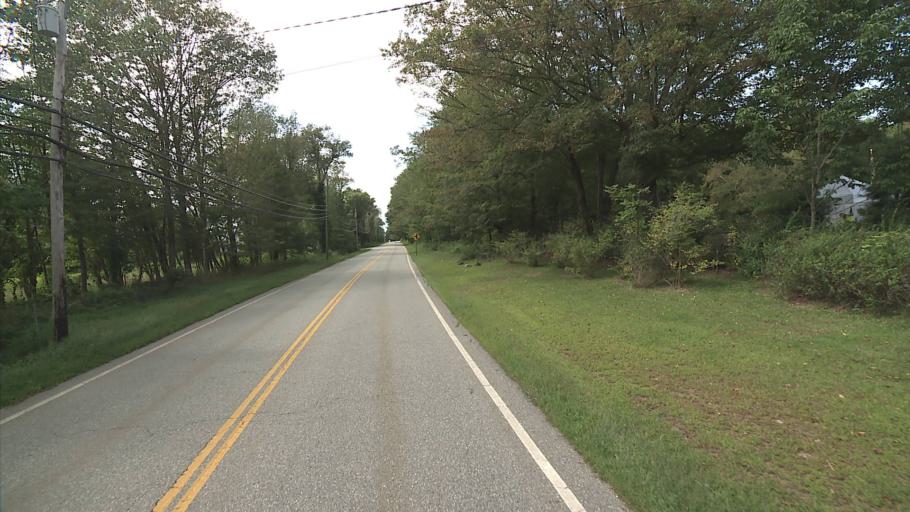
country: US
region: Connecticut
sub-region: New London County
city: Colchester
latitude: 41.6202
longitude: -72.2570
